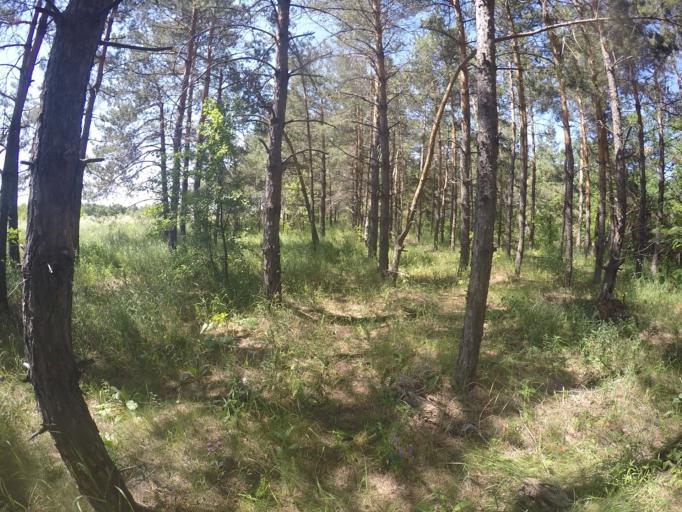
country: RU
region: Saratov
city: Krasnyy Oktyabr'
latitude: 51.3117
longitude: 45.5734
